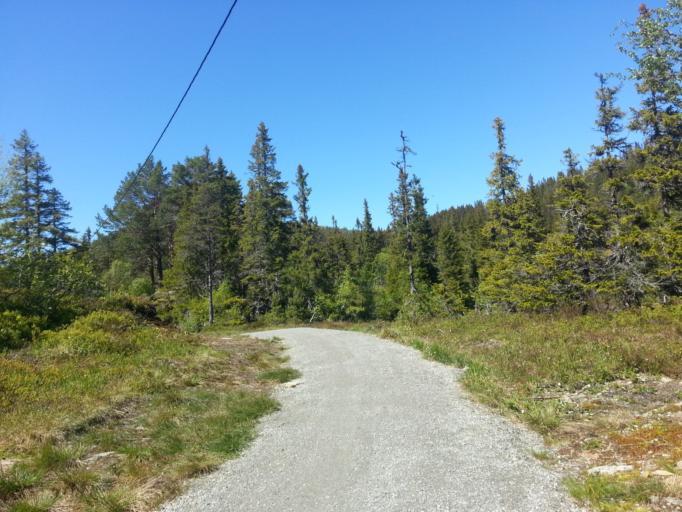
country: NO
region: Sor-Trondelag
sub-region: Melhus
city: Melhus
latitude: 63.4134
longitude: 10.2677
